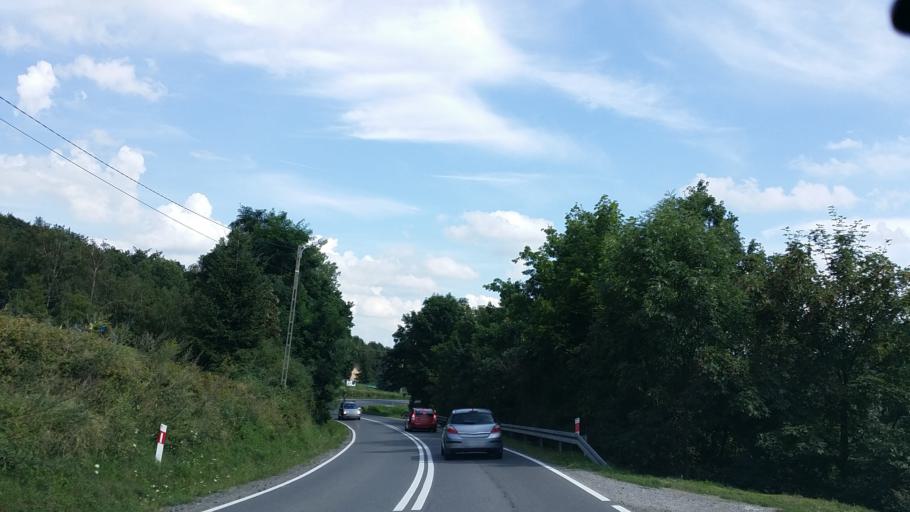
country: PL
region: Lesser Poland Voivodeship
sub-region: Powiat wielicki
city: Pawlikowice
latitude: 49.9327
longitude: 20.0640
